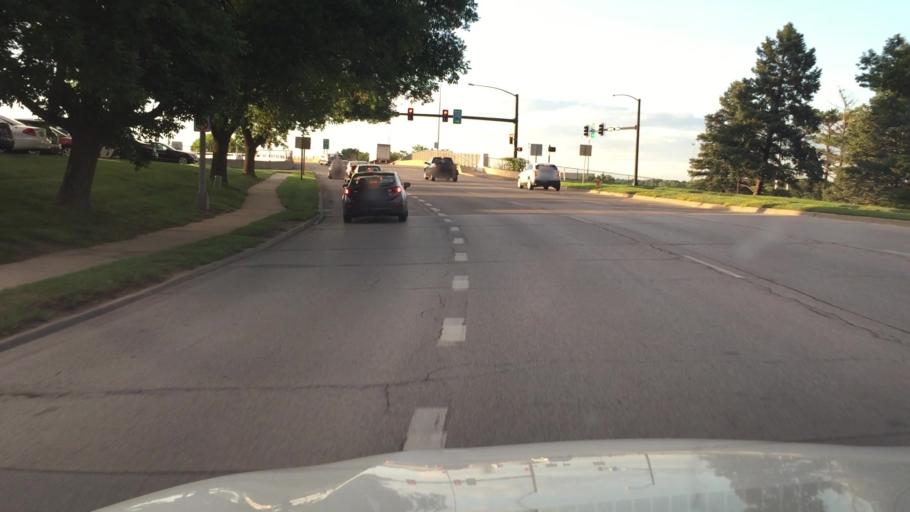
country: US
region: Iowa
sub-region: Polk County
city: Des Moines
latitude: 41.5945
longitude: -93.6200
